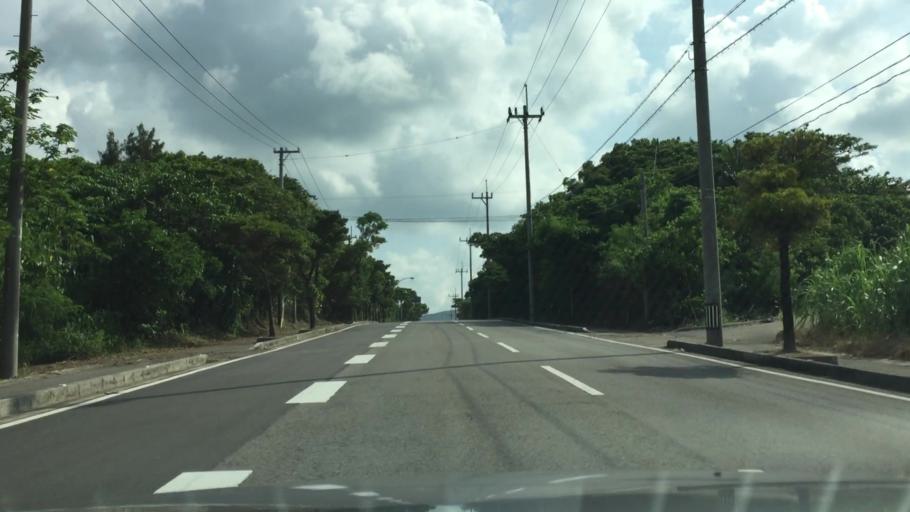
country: JP
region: Okinawa
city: Ishigaki
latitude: 24.4720
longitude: 124.2542
